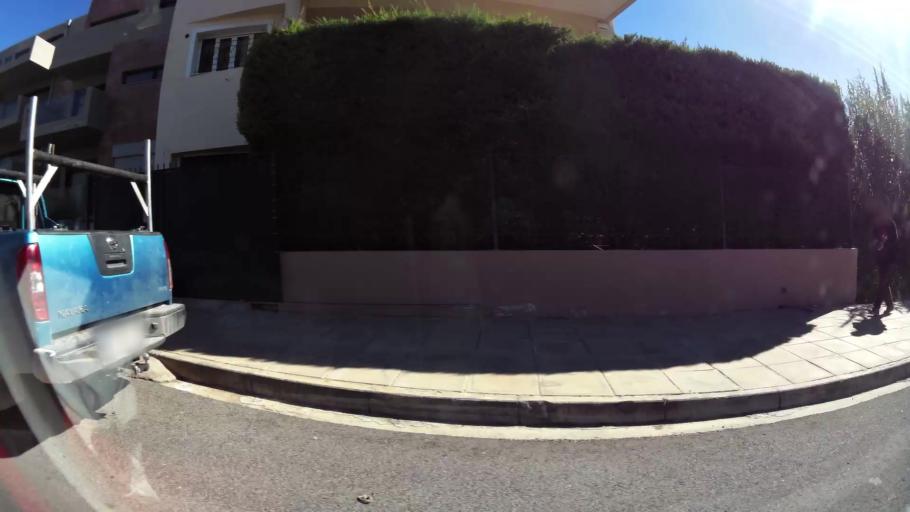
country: GR
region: Attica
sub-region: Nomarchia Anatolikis Attikis
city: Leondarion
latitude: 38.0009
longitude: 23.8549
